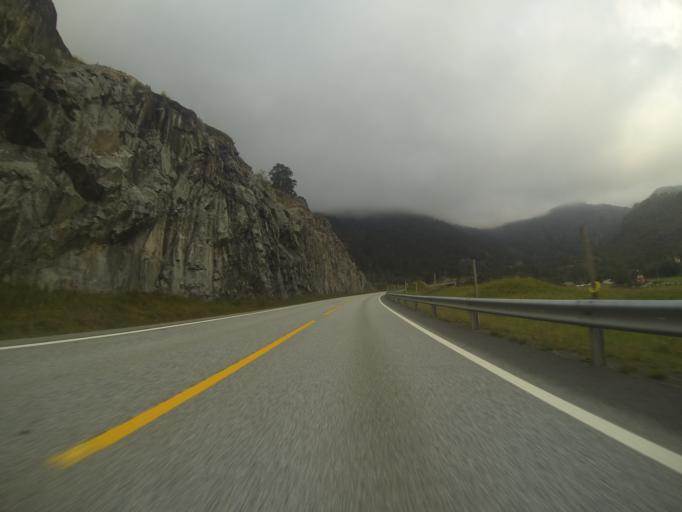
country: NO
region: Hordaland
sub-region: Odda
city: Odda
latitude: 59.8792
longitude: 6.4266
